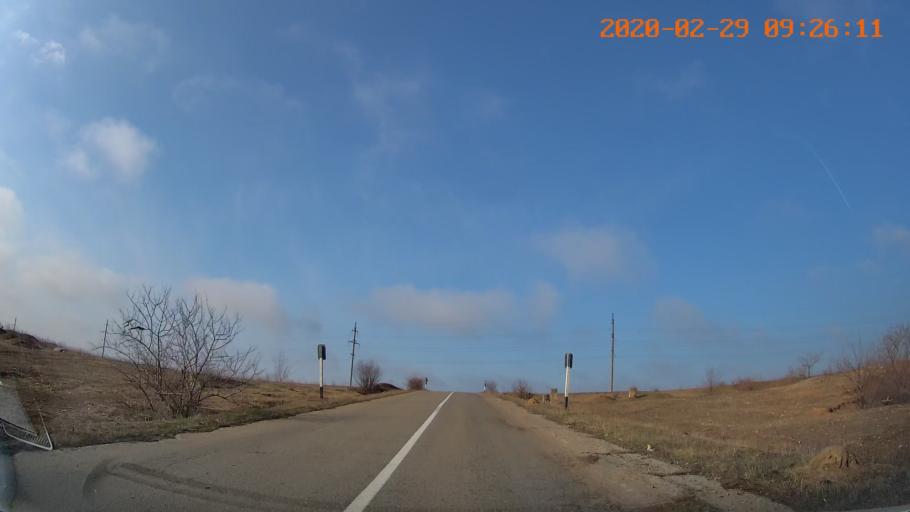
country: MD
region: Telenesti
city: Pervomaisc
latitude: 46.7046
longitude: 29.9511
